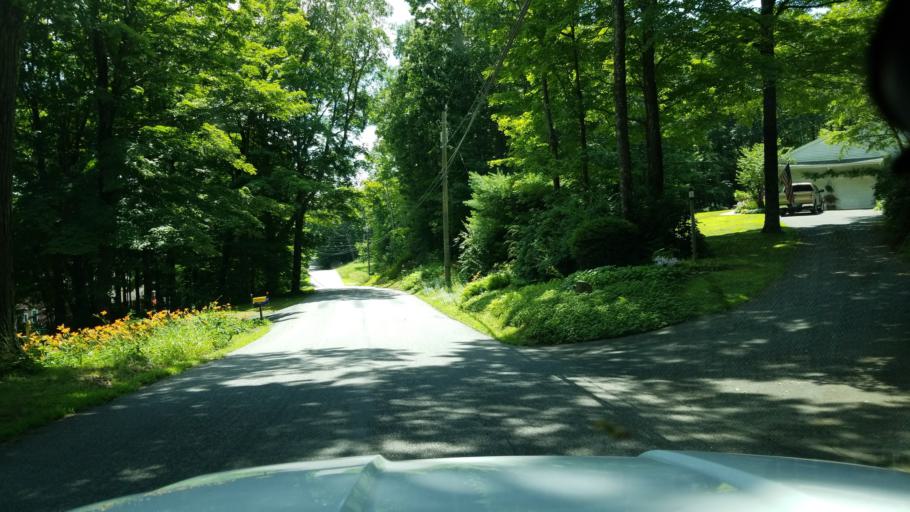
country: US
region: Massachusetts
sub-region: Hampden County
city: Holland
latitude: 41.9792
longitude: -72.1909
